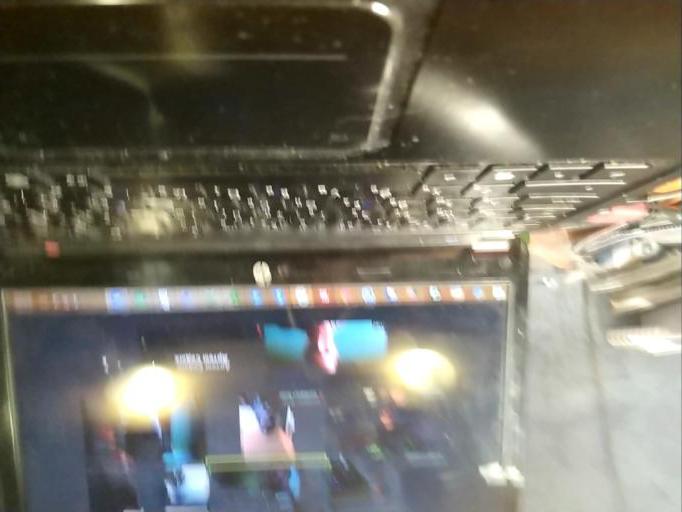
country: RU
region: Tverskaya
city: Ves'yegonsk
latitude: 58.7010
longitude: 37.5439
